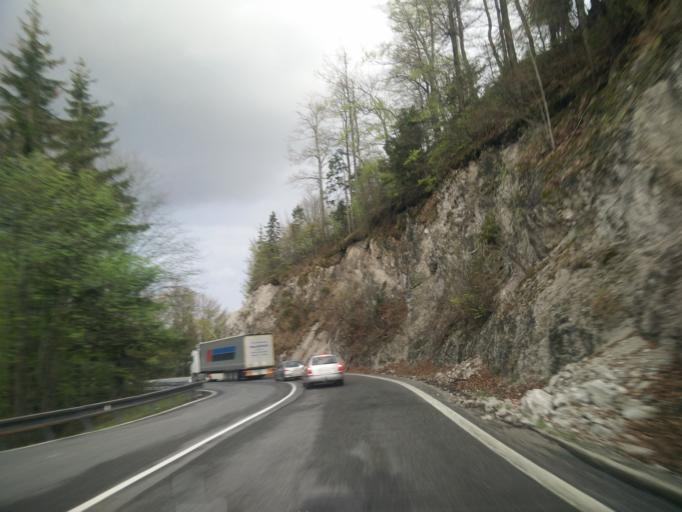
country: SK
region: Banskobystricky
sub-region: Okres Ziar nad Hronom
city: Kremnica
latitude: 48.8349
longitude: 19.0131
